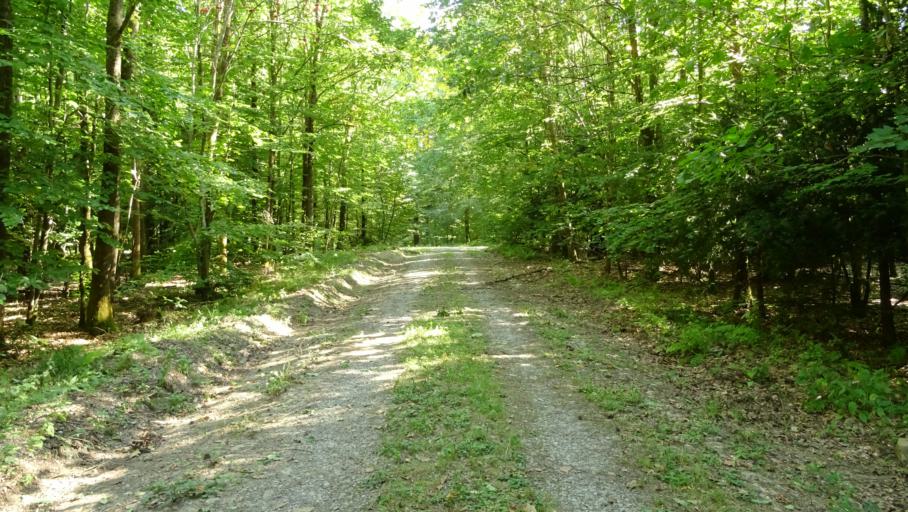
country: DE
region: Baden-Wuerttemberg
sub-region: Karlsruhe Region
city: Fahrenbach
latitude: 49.4113
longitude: 9.1168
